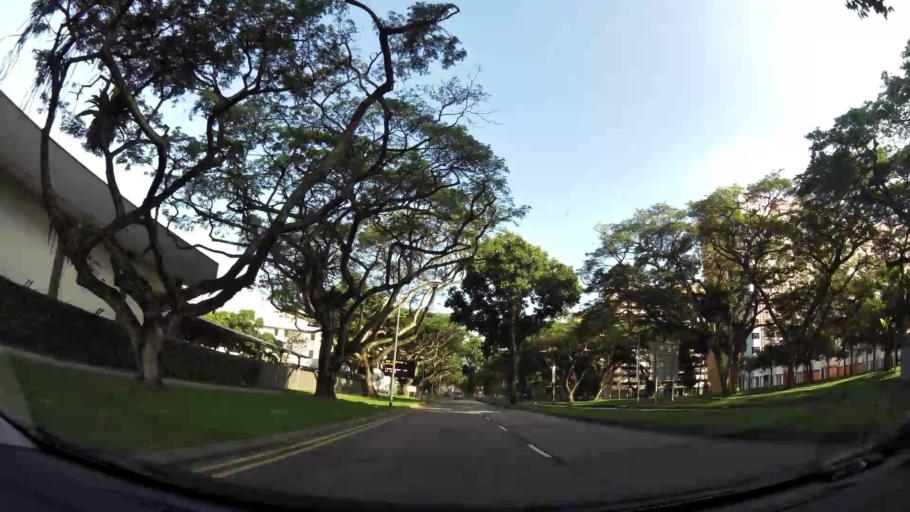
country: SG
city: Singapore
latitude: 1.3205
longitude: 103.9324
